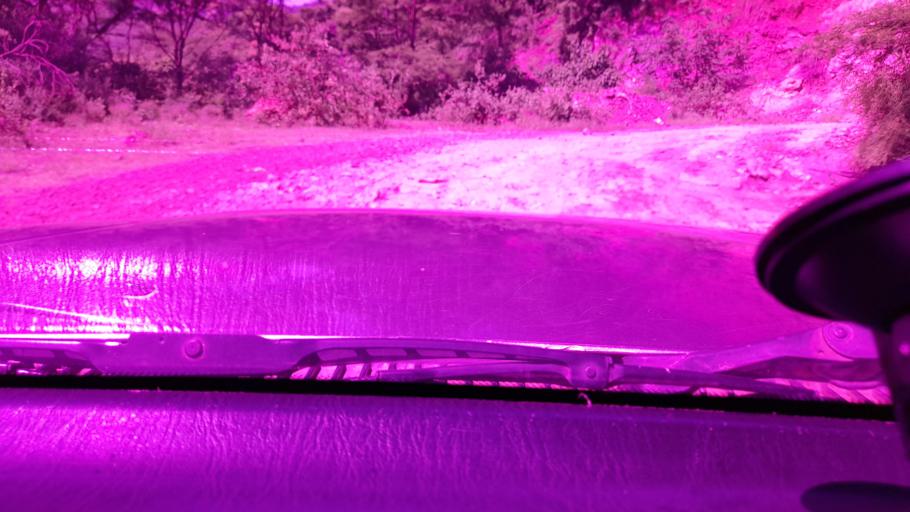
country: ET
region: Oromiya
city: Jima
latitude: 7.7994
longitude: 37.5247
